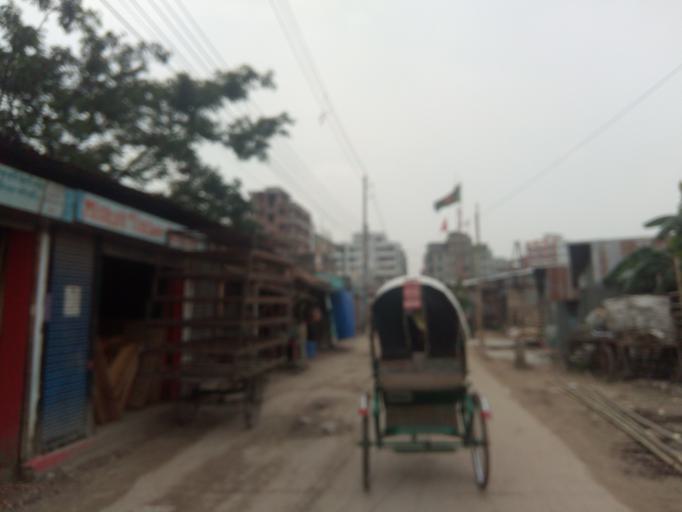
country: BD
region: Dhaka
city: Paltan
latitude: 23.7574
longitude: 90.4292
